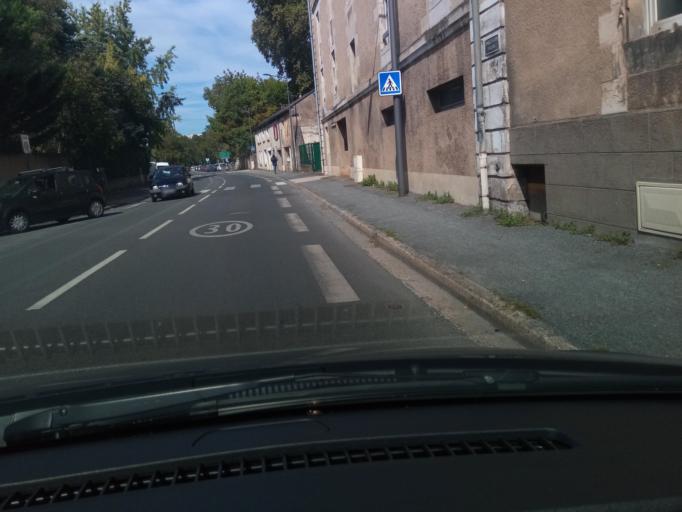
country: FR
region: Poitou-Charentes
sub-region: Departement de la Vienne
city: Poitiers
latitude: 46.5834
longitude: 0.3522
